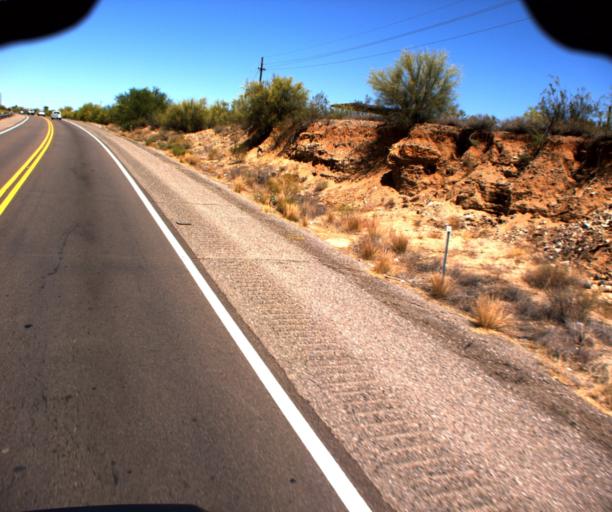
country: US
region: Arizona
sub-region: Maricopa County
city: Wickenburg
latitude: 33.9955
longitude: -112.7552
